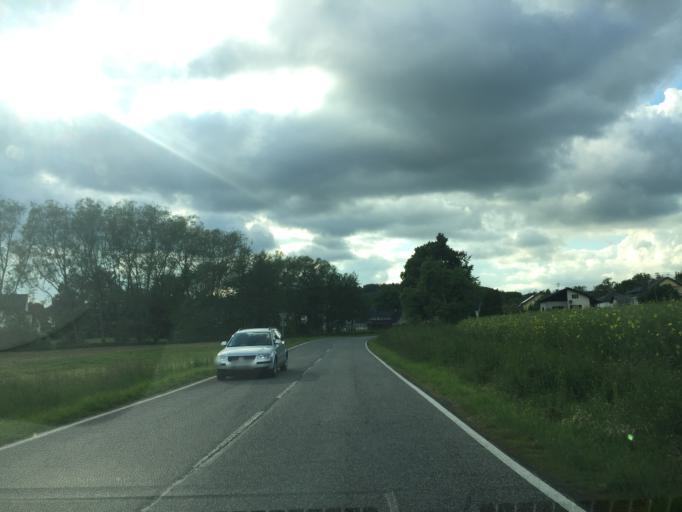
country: DE
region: Rheinland-Pfalz
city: Meudt
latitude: 50.4987
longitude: 7.9077
